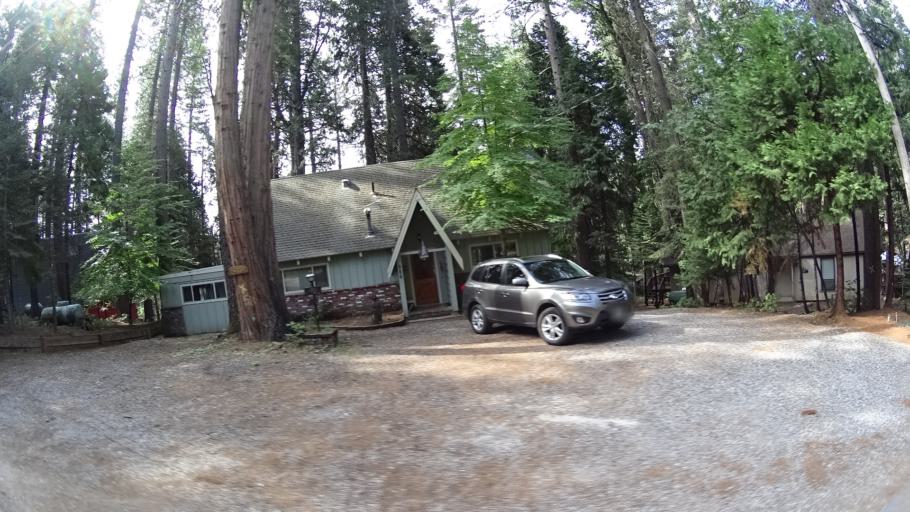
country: US
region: California
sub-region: Calaveras County
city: Arnold
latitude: 38.2551
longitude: -120.3331
